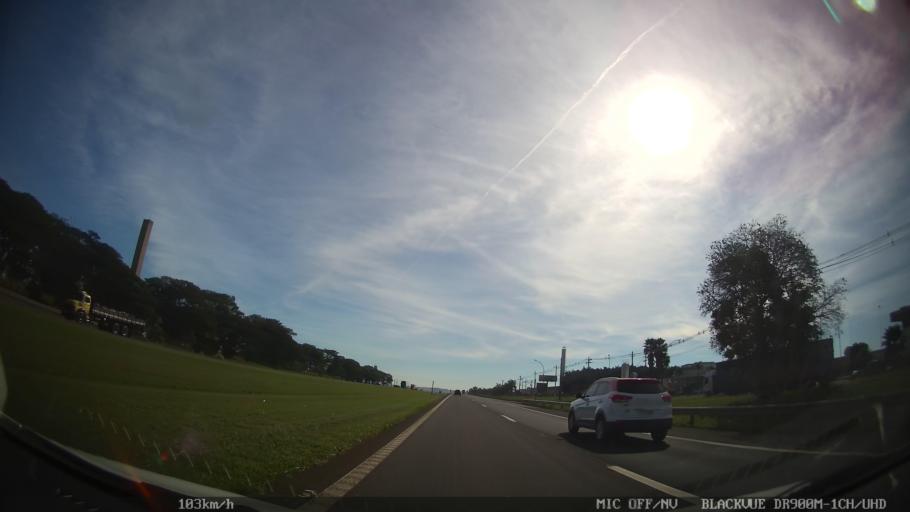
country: BR
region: Sao Paulo
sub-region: Araras
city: Araras
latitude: -22.4100
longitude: -47.3898
